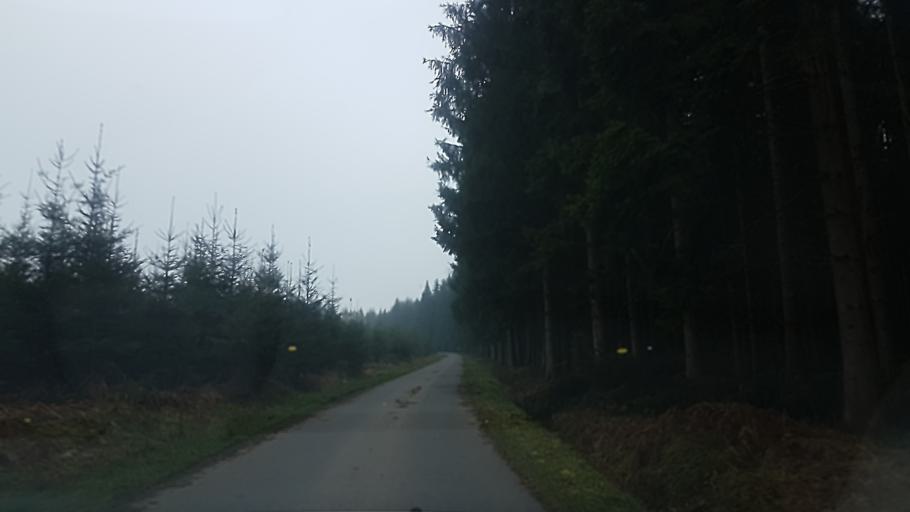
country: FR
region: Champagne-Ardenne
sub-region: Departement des Ardennes
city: Haybes
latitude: 50.0477
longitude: 4.6672
